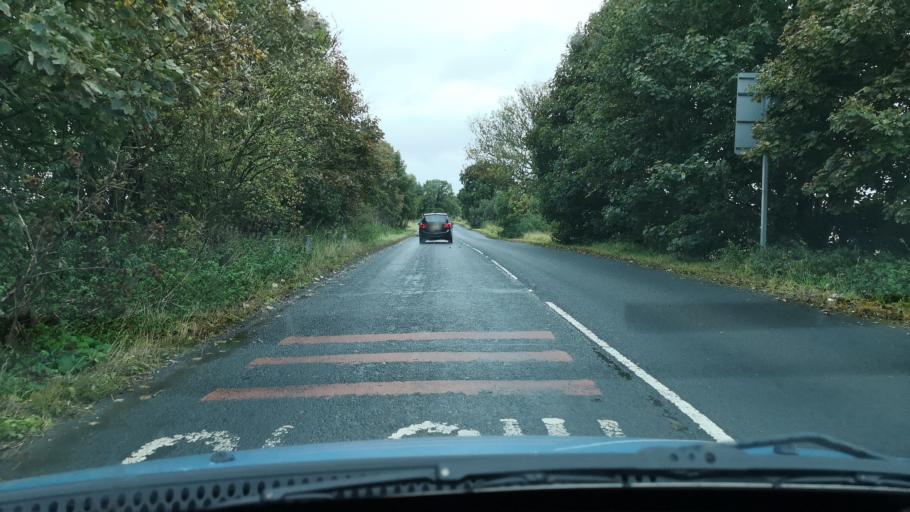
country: GB
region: England
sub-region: Doncaster
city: Hatfield
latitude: 53.6013
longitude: -0.9660
